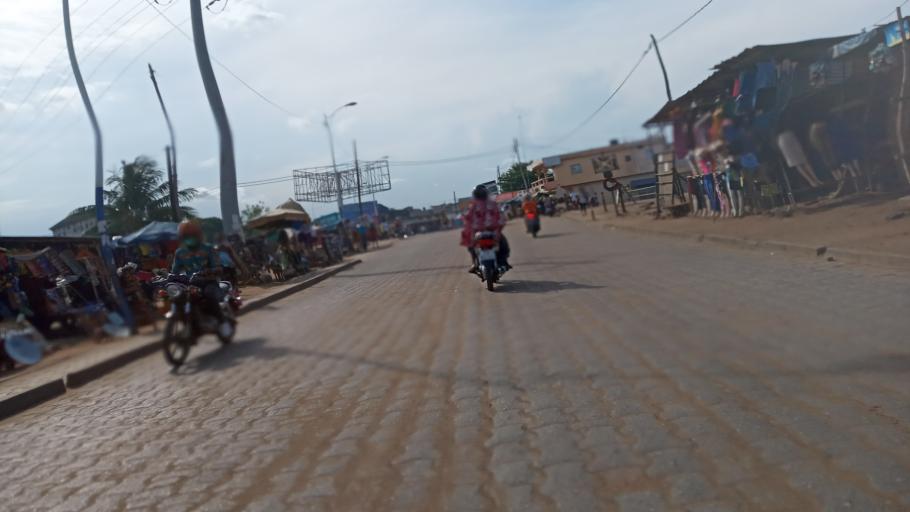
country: TG
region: Maritime
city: Lome
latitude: 6.1559
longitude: 1.2672
